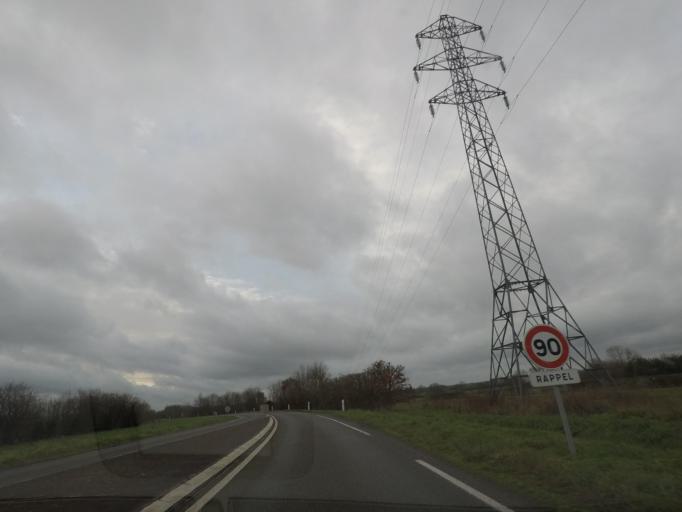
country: FR
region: Pays de la Loire
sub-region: Departement de la Sarthe
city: La Ferte-Bernard
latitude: 48.1906
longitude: 0.6270
